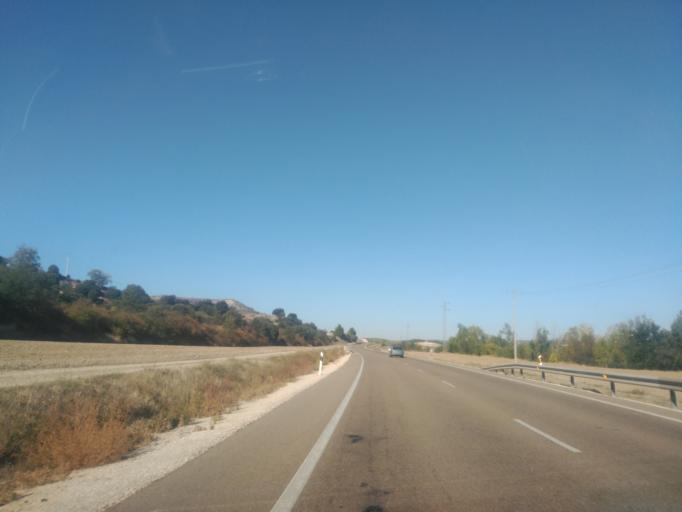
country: ES
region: Castille and Leon
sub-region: Provincia de Valladolid
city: Quintanilla de Arriba
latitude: 41.6225
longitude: -4.2485
